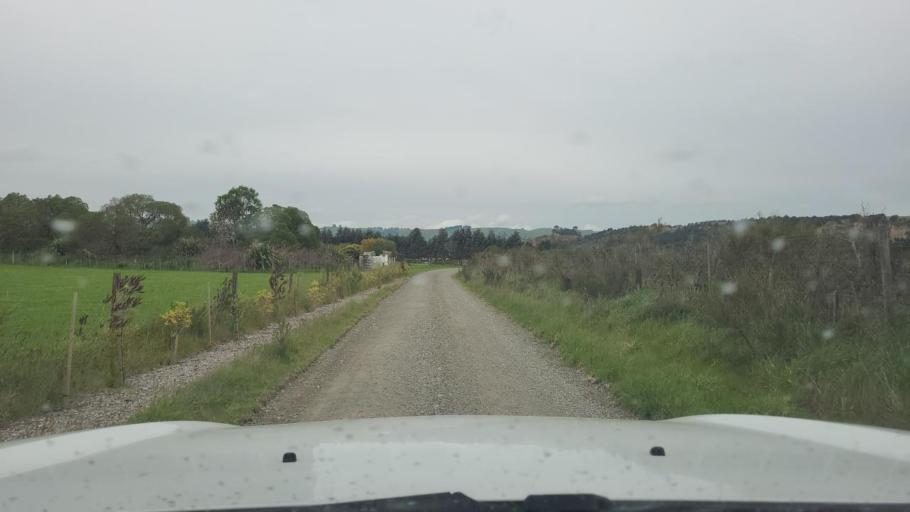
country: NZ
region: Wellington
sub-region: Masterton District
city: Masterton
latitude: -41.0711
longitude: 175.6185
